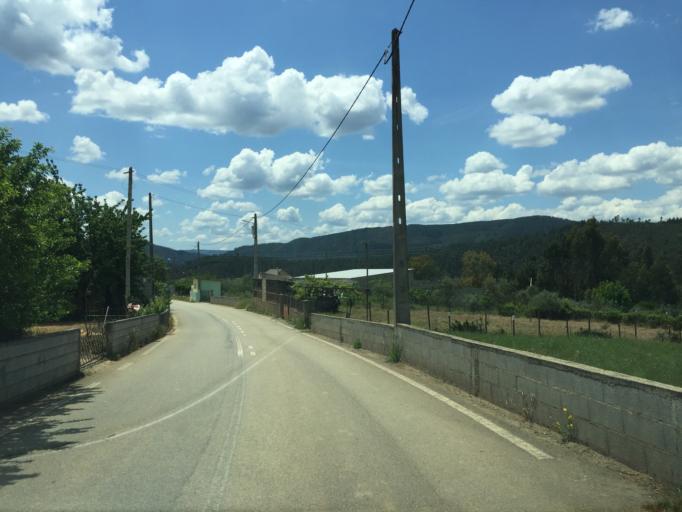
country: PT
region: Coimbra
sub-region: Pampilhosa da Serra
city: Pampilhosa da Serra
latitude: 40.0732
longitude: -7.7998
